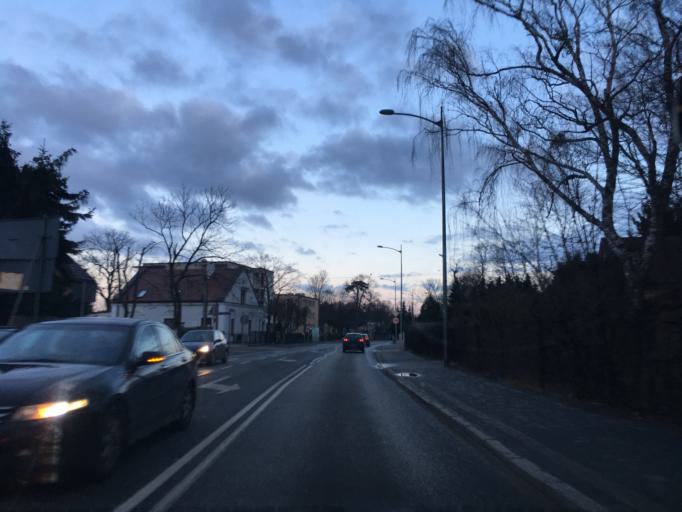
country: PL
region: Masovian Voivodeship
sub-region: Powiat grodziski
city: Grodzisk Mazowiecki
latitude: 52.1047
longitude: 20.6347
